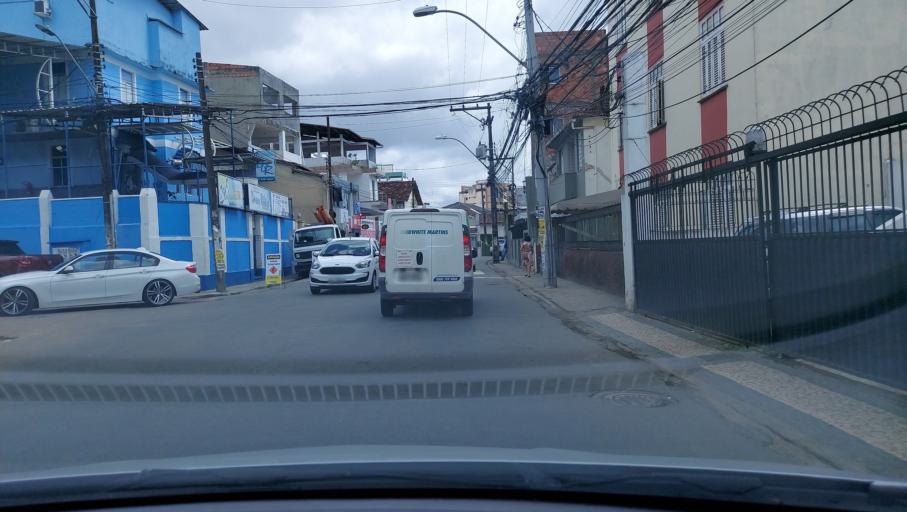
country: BR
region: Bahia
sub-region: Salvador
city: Salvador
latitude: -12.9745
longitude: -38.4939
